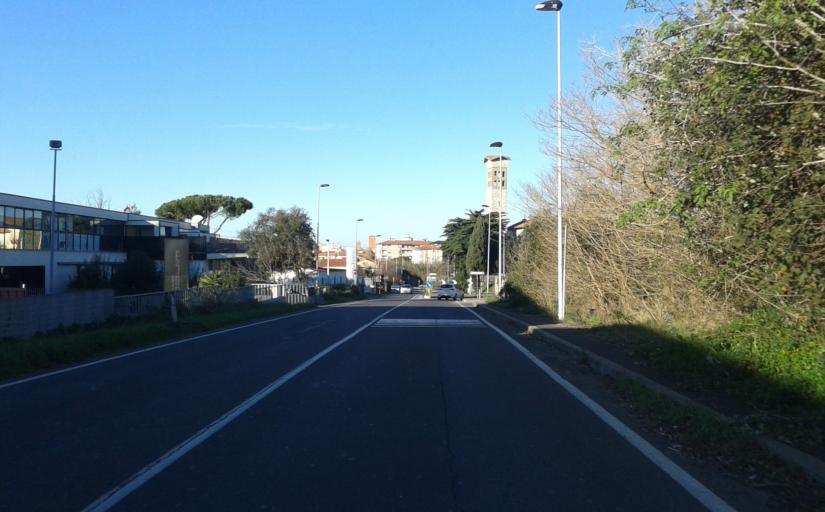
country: IT
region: Tuscany
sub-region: Provincia di Livorno
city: Livorno
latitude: 43.5112
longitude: 10.3269
